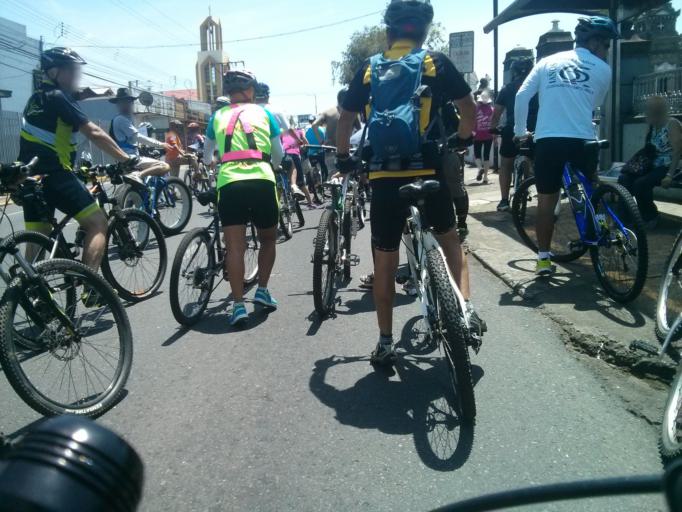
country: CR
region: San Jose
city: San Jose
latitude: 9.9302
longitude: -84.0902
